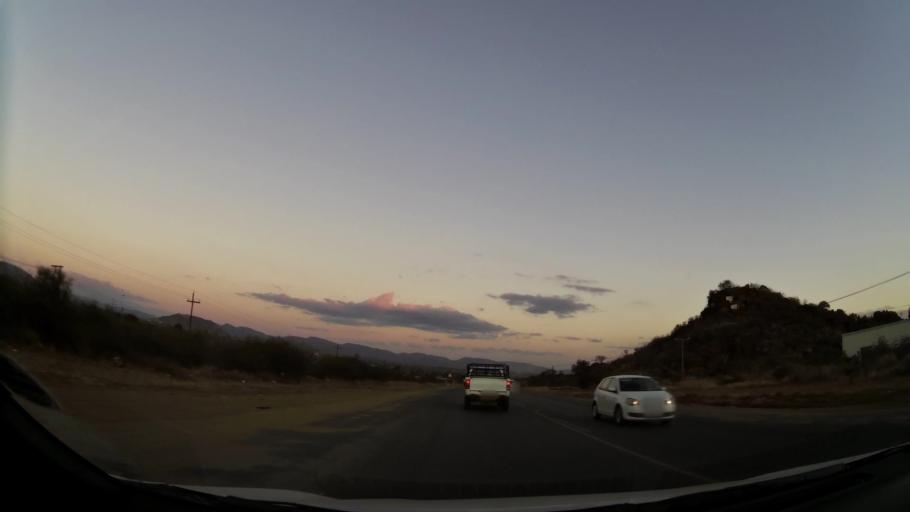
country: ZA
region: Limpopo
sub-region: Waterberg District Municipality
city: Mokopane
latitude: -24.1547
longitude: 28.9775
